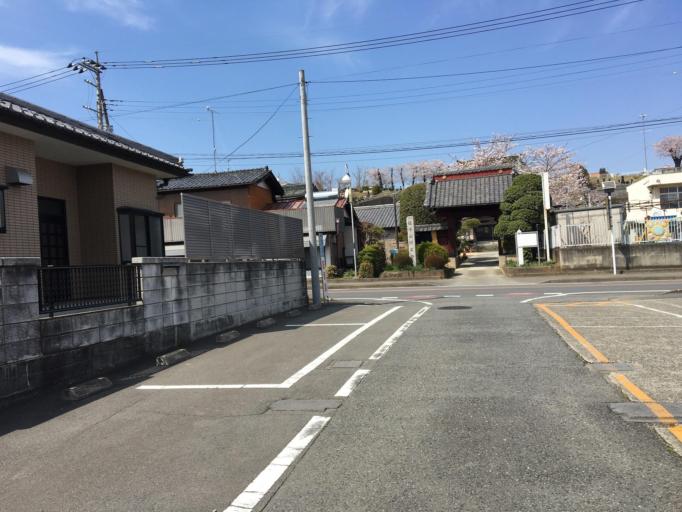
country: JP
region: Gunma
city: Annaka
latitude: 36.3377
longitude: 138.9299
